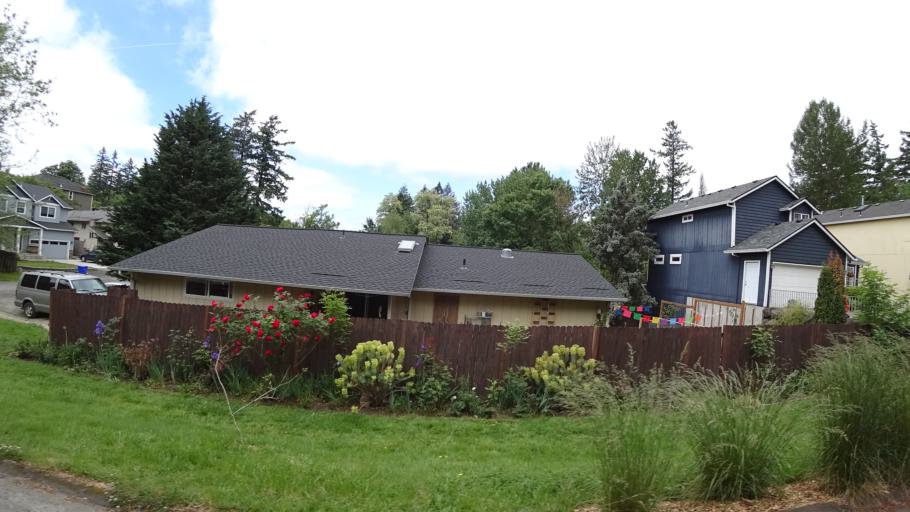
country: US
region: Oregon
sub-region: Washington County
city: Garden Home-Whitford
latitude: 45.4563
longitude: -122.7254
